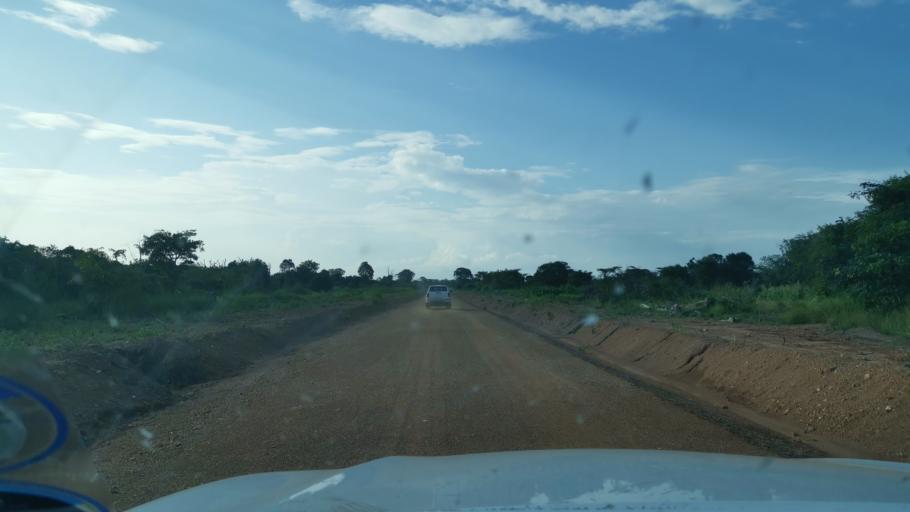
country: ZM
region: Luapula
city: Samfya
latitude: -11.1146
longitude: 29.5777
